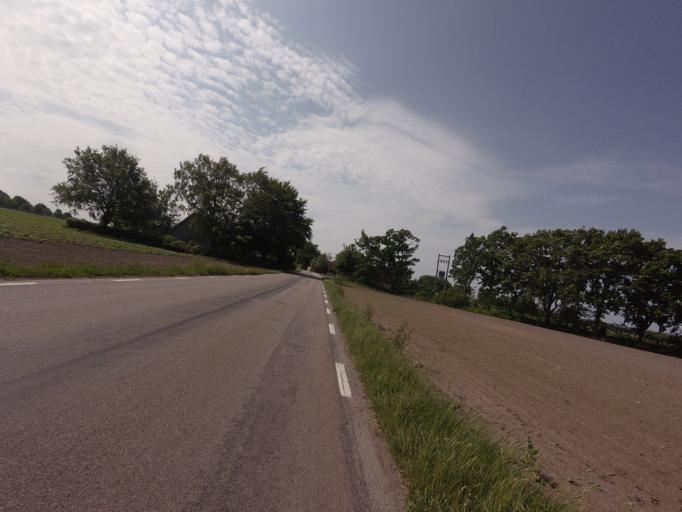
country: SE
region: Skane
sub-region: Helsingborg
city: Odakra
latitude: 56.2040
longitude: 12.7035
